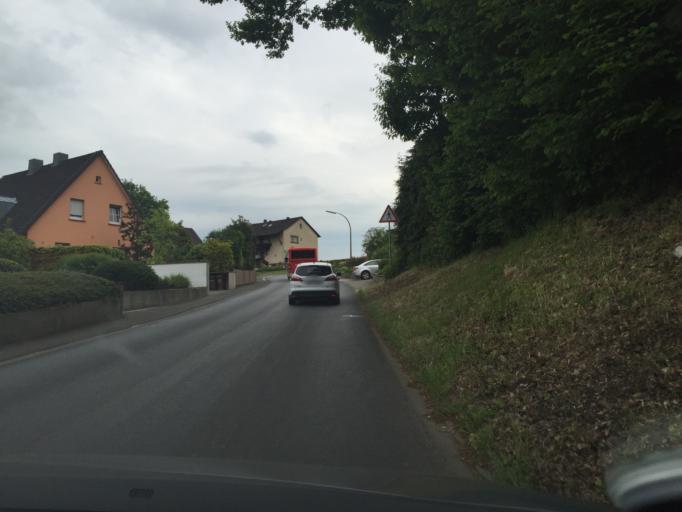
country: DE
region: Bavaria
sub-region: Regierungsbezirk Unterfranken
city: Hosbach
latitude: 50.0273
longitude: 9.1894
